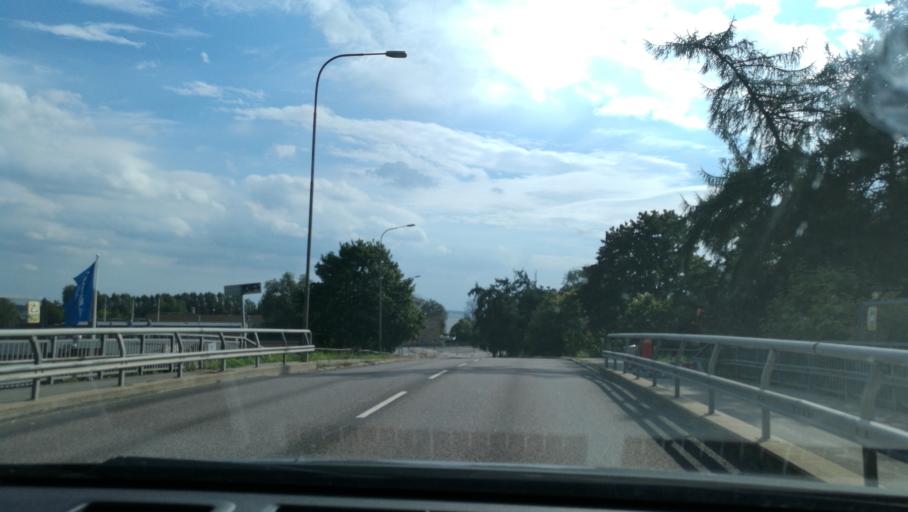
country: SE
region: Vaestmanland
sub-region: Vasteras
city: Vasteras
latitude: 59.5980
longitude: 16.5243
